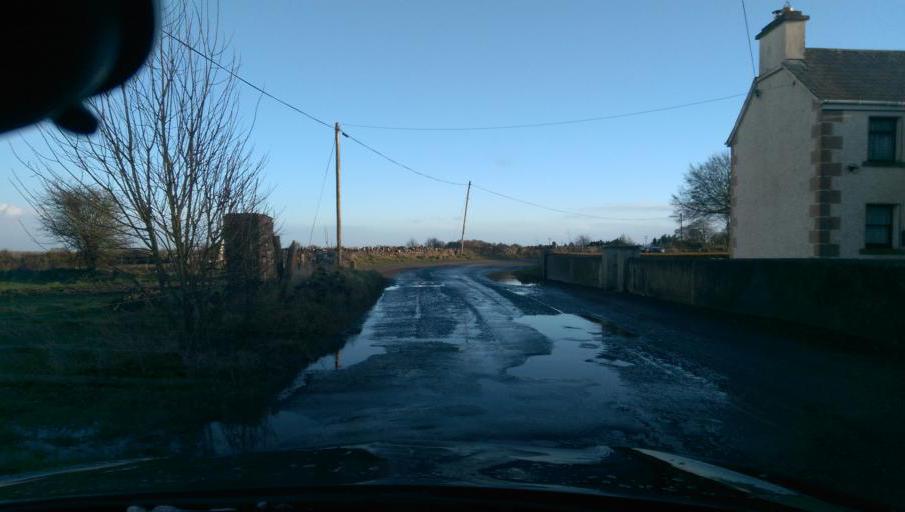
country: IE
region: Connaught
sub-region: County Galway
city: Loughrea
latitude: 53.4093
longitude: -8.4980
